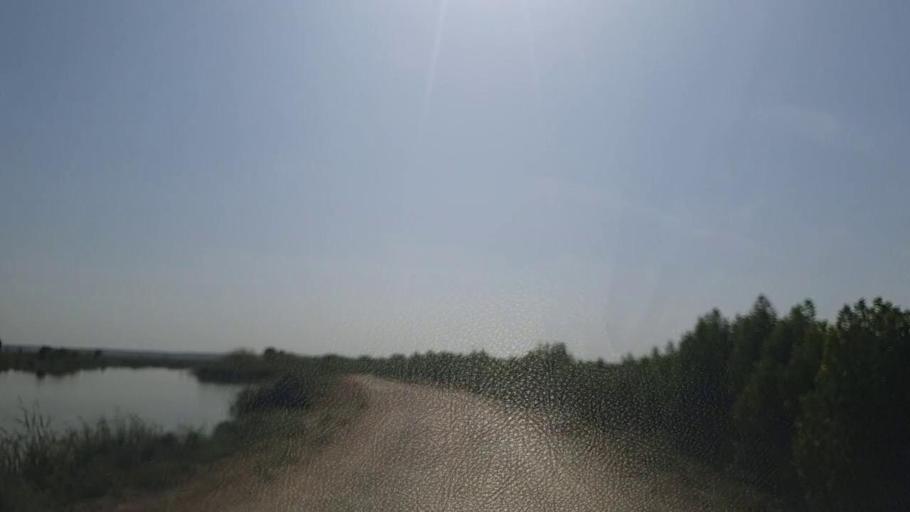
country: PK
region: Sindh
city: Thatta
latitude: 24.6404
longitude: 67.8796
